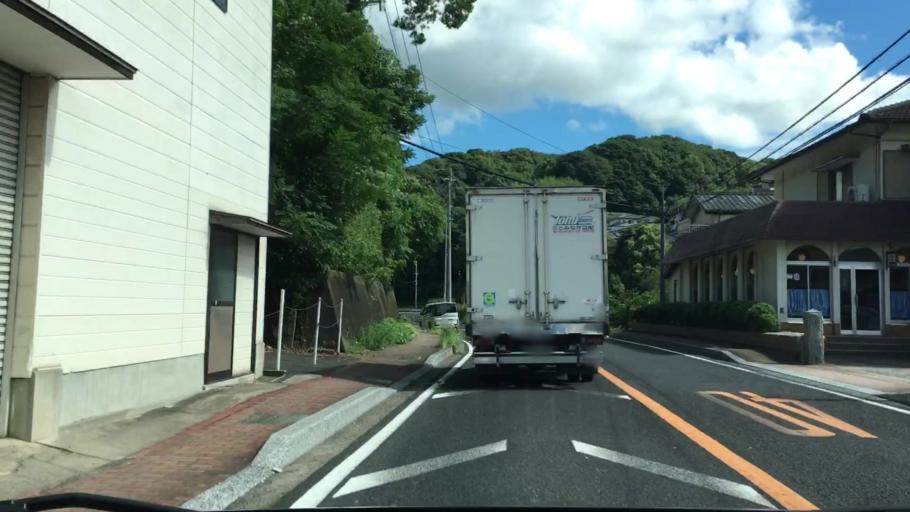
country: JP
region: Nagasaki
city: Sasebo
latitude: 33.1396
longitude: 129.7879
